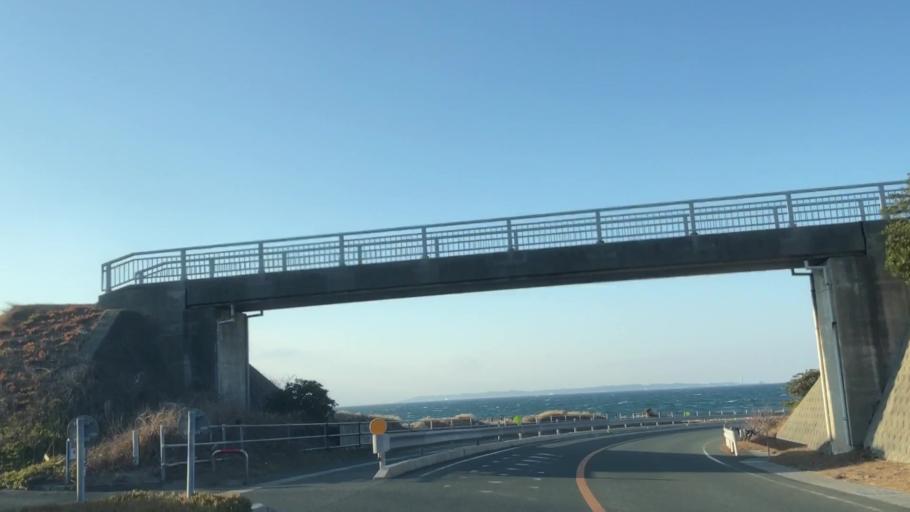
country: JP
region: Aichi
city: Toyohama
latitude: 34.5884
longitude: 137.0274
